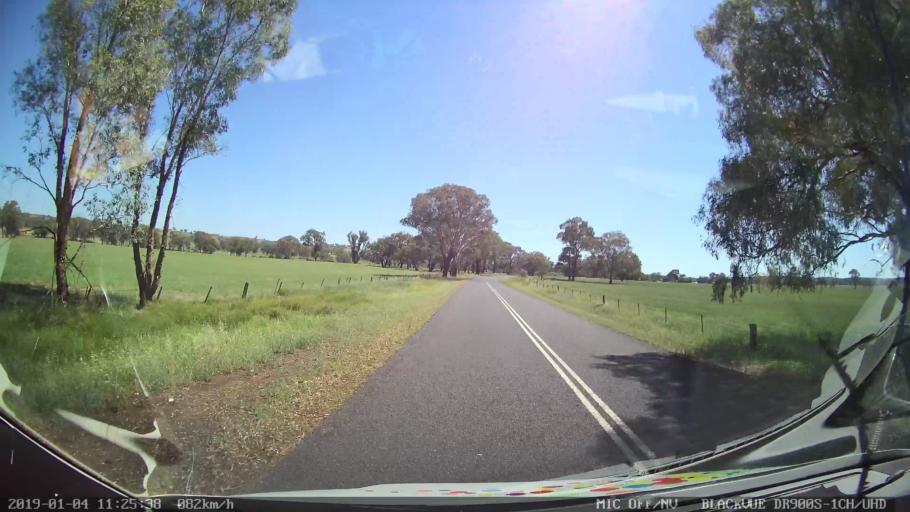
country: AU
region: New South Wales
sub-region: Cabonne
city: Molong
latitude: -33.1224
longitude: 148.7525
